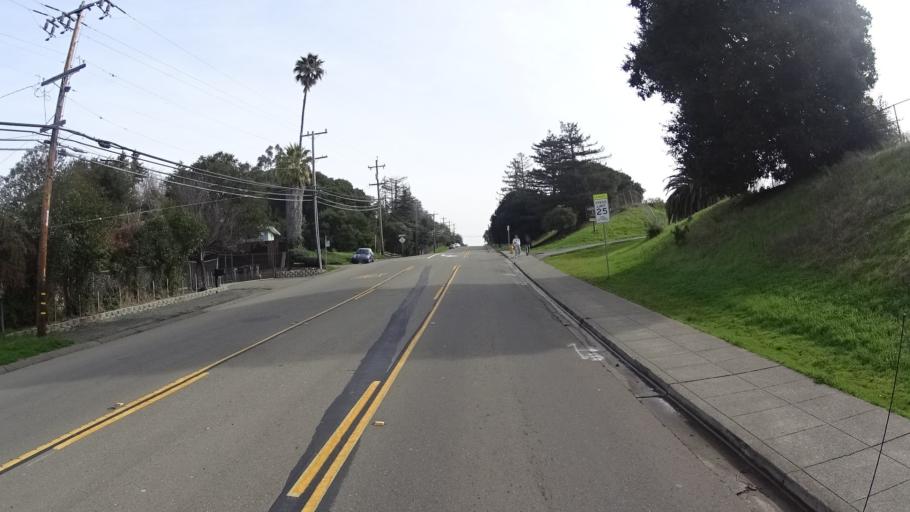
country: US
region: California
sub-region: Alameda County
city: Hayward
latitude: 37.6729
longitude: -122.0720
